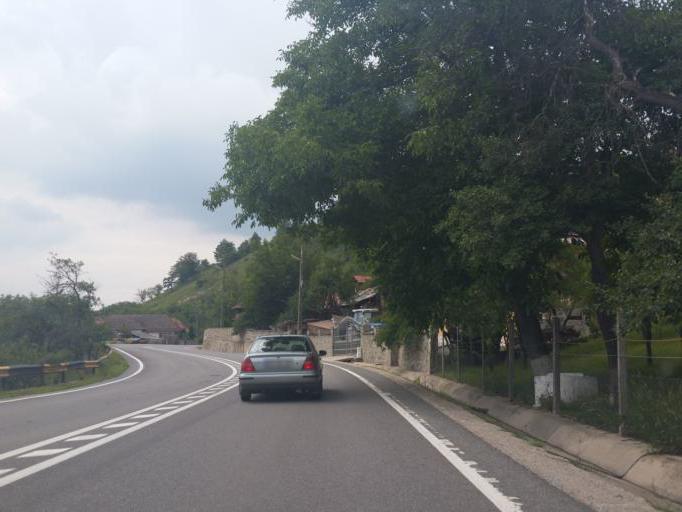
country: RO
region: Salaj
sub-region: Comuna Treznea
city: Treznea
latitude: 47.1244
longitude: 23.1350
